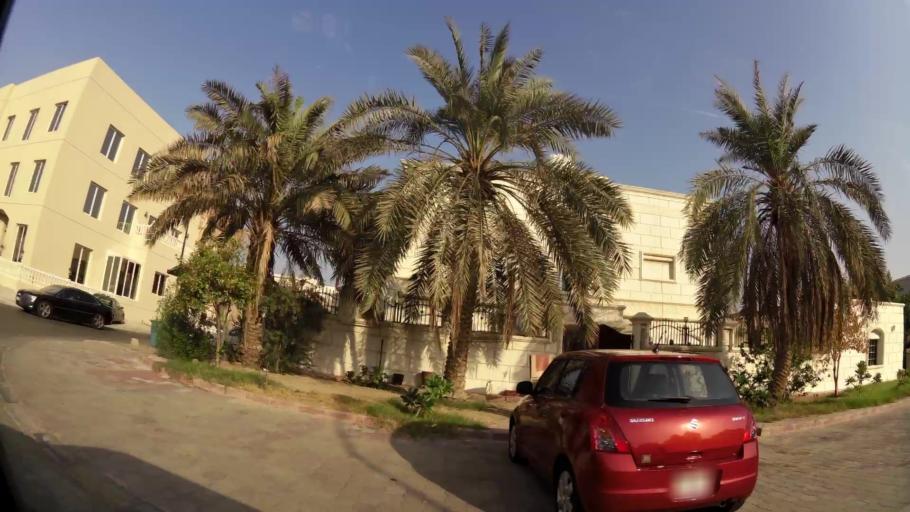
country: KW
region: Muhafazat Hawalli
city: Ar Rumaythiyah
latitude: 29.3211
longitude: 48.0825
